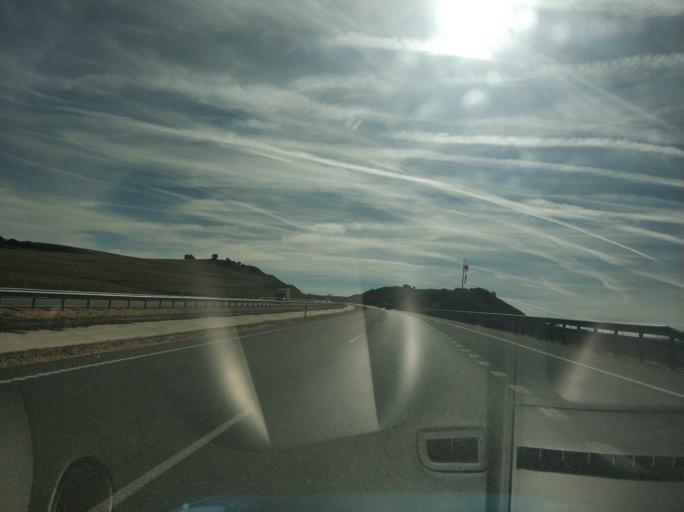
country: ES
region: Castille and Leon
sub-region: Provincia de Zamora
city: Corrales
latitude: 41.3307
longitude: -5.7269
